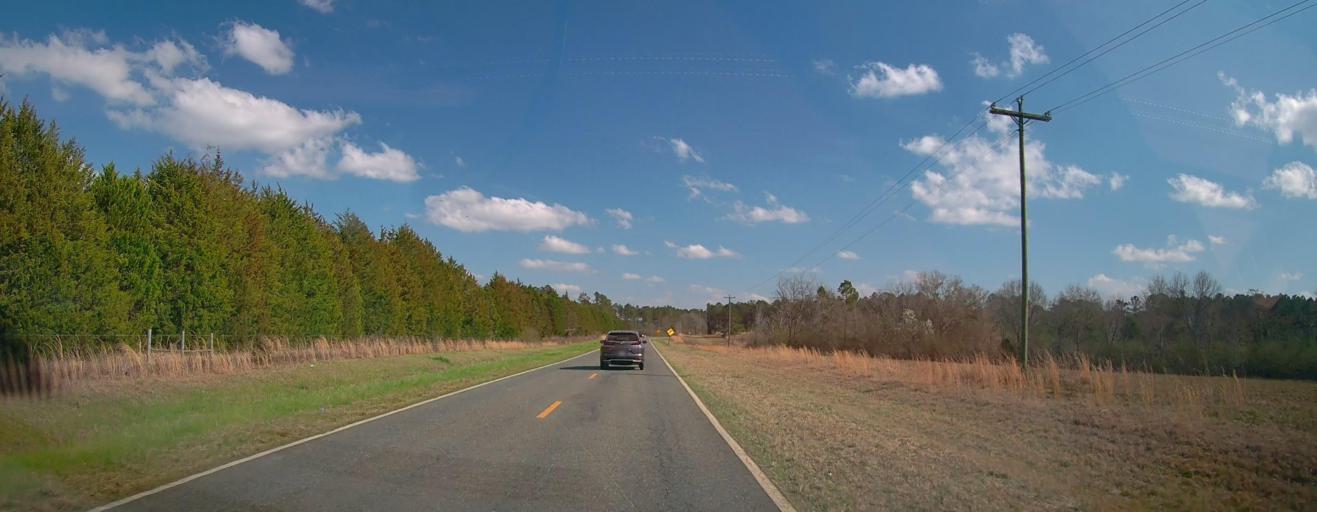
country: US
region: Georgia
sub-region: Laurens County
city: Dublin
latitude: 32.5874
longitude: -83.0597
